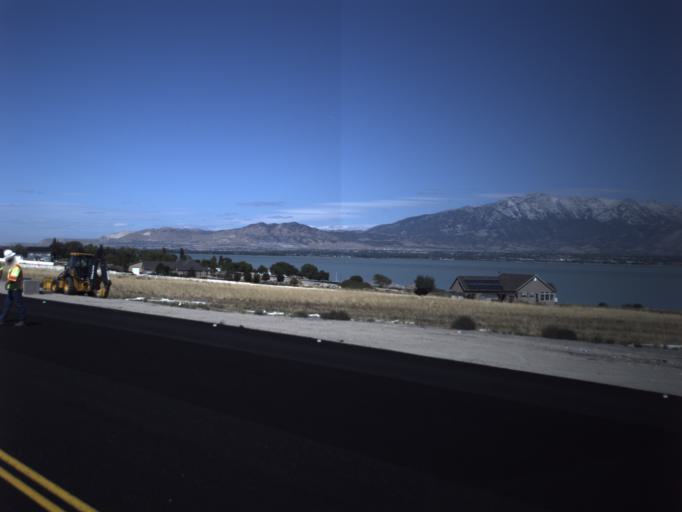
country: US
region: Utah
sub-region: Utah County
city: Saratoga Springs
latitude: 40.2957
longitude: -111.8819
